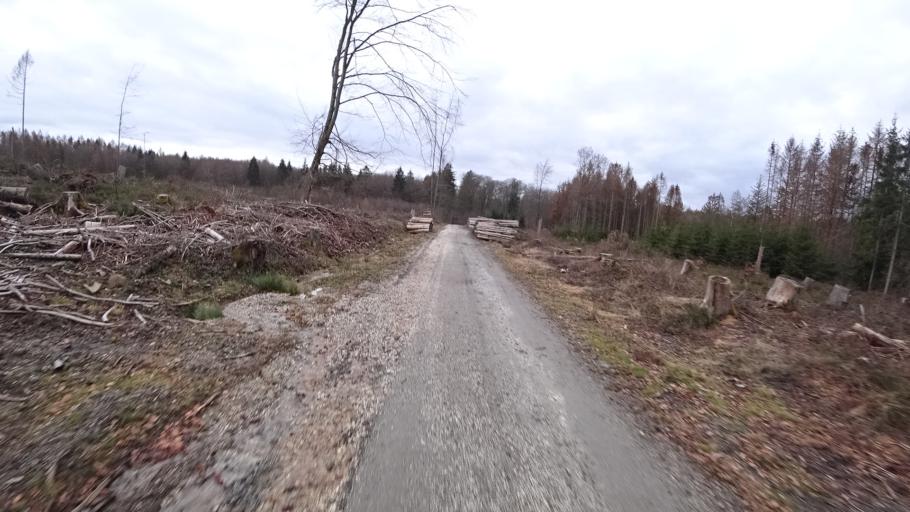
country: DE
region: Rheinland-Pfalz
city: Hilgert
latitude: 50.4381
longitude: 7.7058
